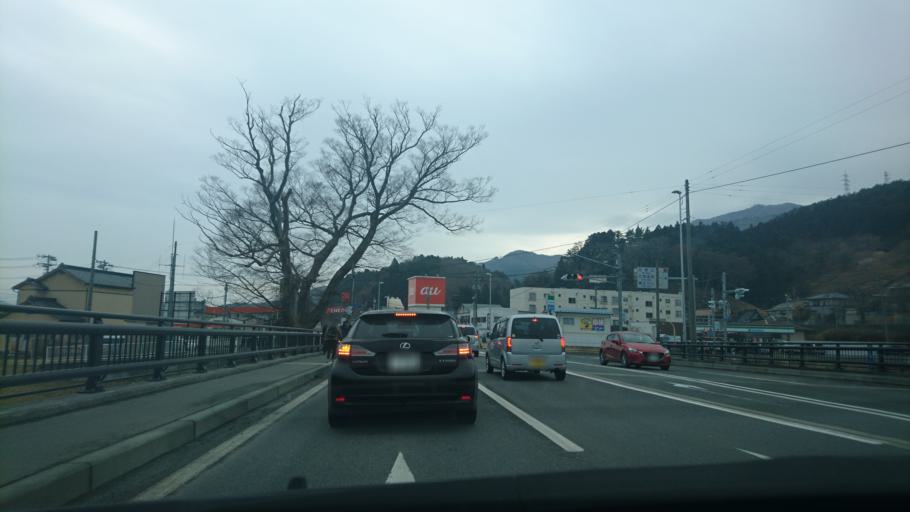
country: JP
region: Iwate
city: Ofunato
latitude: 39.0919
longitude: 141.7062
